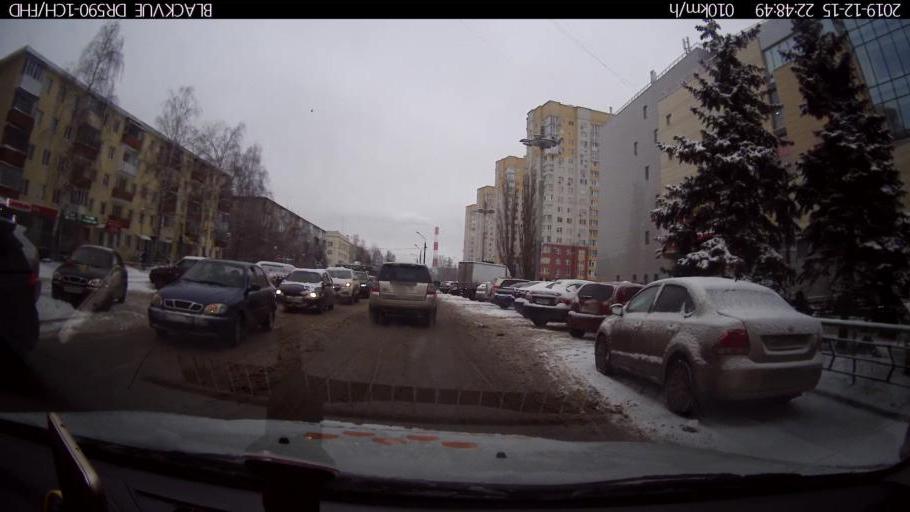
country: RU
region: Nizjnij Novgorod
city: Neklyudovo
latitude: 56.3481
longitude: 43.8701
